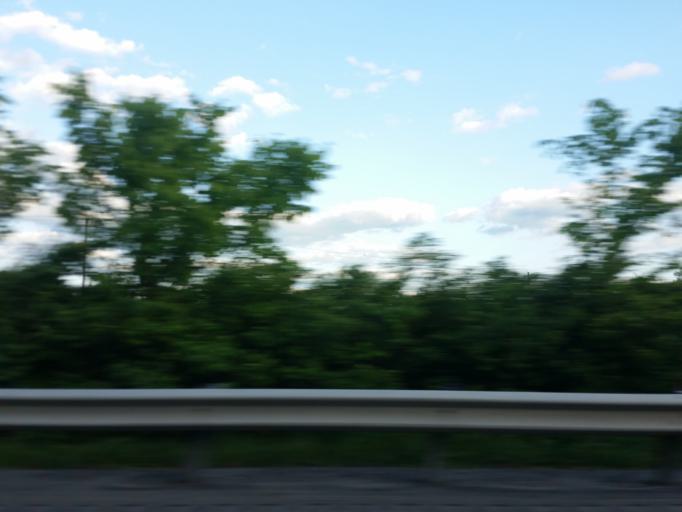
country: US
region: Virginia
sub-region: Washington County
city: Abingdon
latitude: 36.6601
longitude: -82.0661
